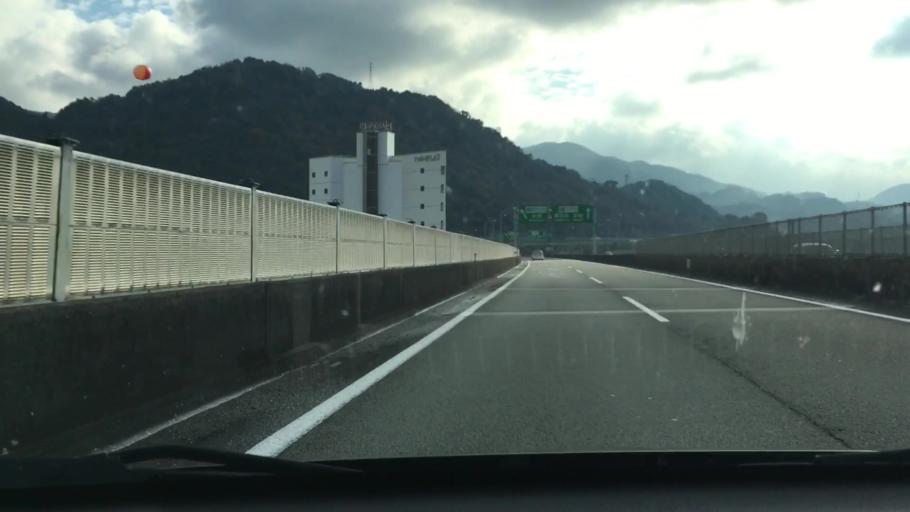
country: JP
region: Kumamoto
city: Yatsushiro
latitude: 32.5079
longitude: 130.6466
